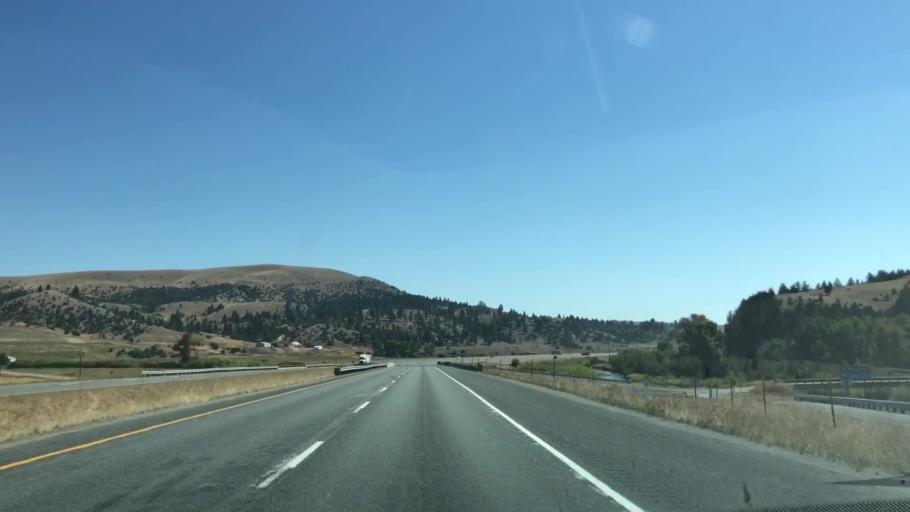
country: US
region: Montana
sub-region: Powell County
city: Deer Lodge
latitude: 46.5570
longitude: -112.8709
